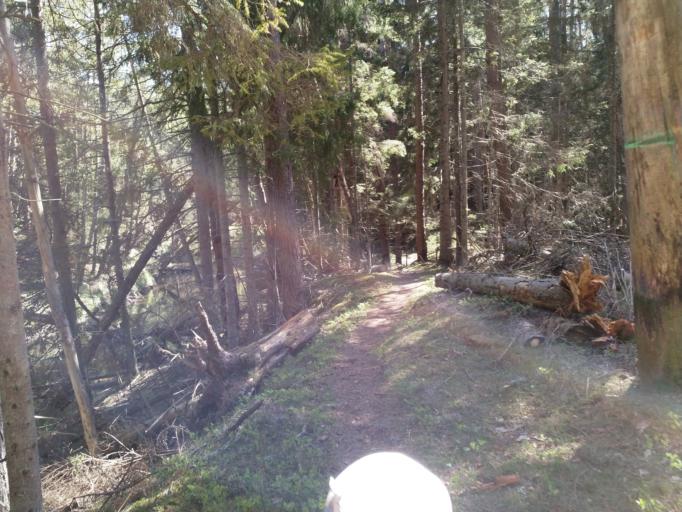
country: LV
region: Pavilostas
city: Pavilosta
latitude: 56.9613
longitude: 21.3559
